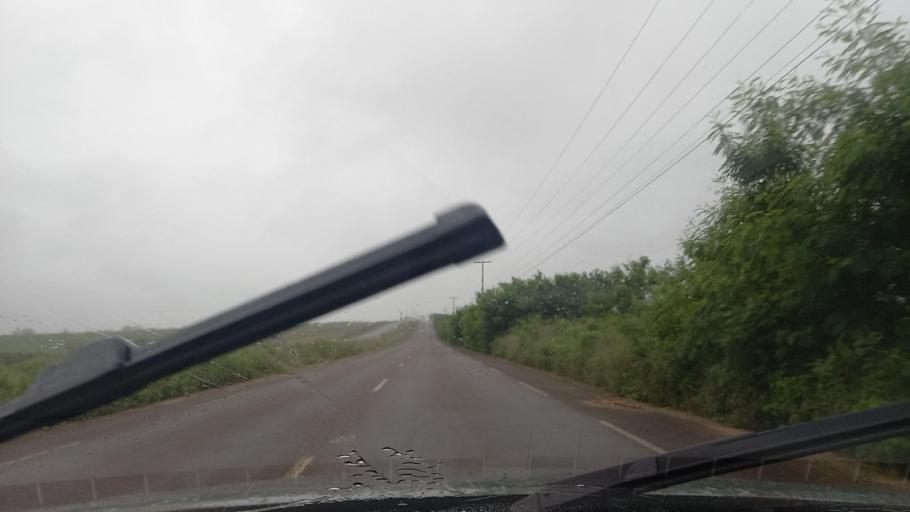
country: BR
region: Alagoas
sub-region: Lagoa Da Canoa
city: Lagoa da Canoa
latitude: -9.6970
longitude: -36.8089
